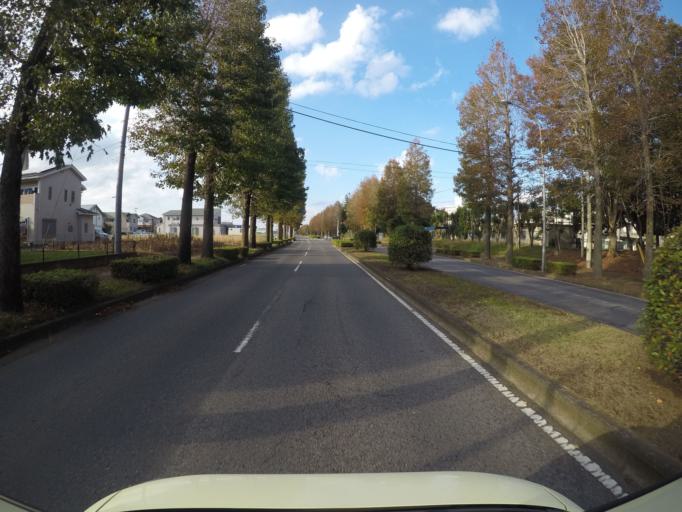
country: JP
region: Ibaraki
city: Naka
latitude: 36.0626
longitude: 140.1020
